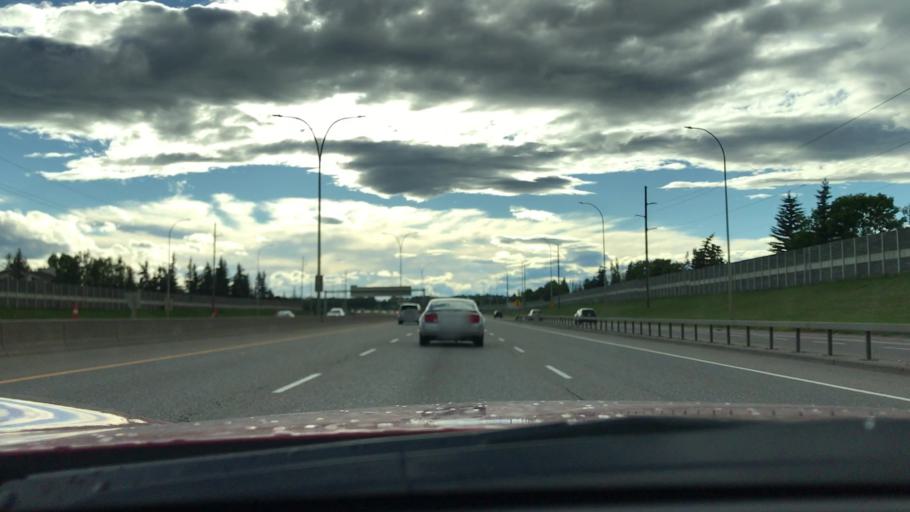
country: CA
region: Alberta
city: Calgary
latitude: 50.9499
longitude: -114.0075
